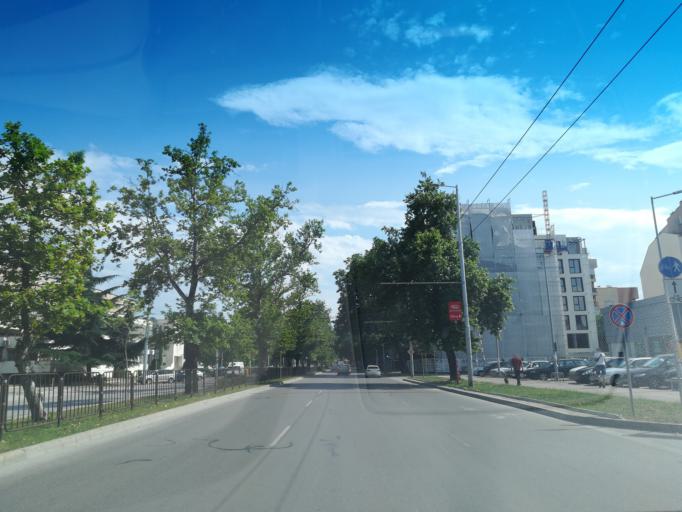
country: BG
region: Plovdiv
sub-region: Obshtina Plovdiv
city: Plovdiv
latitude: 42.1396
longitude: 24.7630
